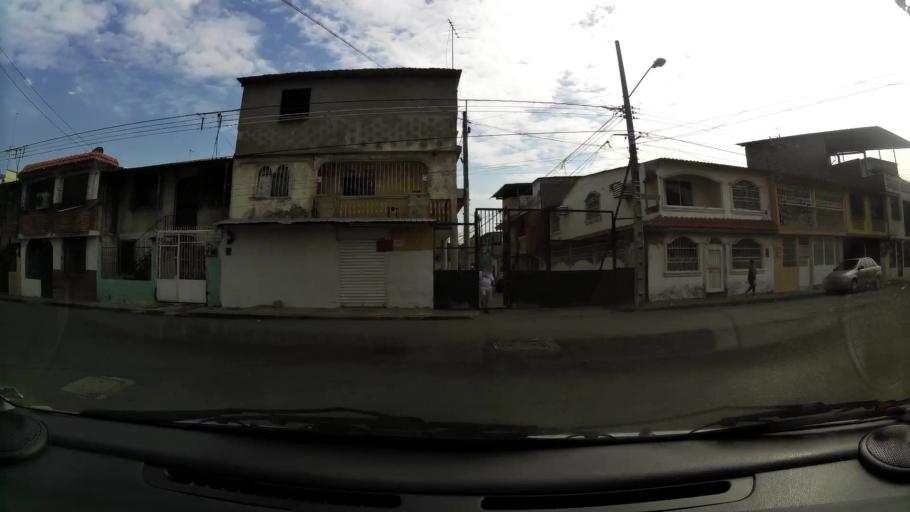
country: EC
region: Guayas
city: Guayaquil
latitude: -2.2437
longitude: -79.8848
